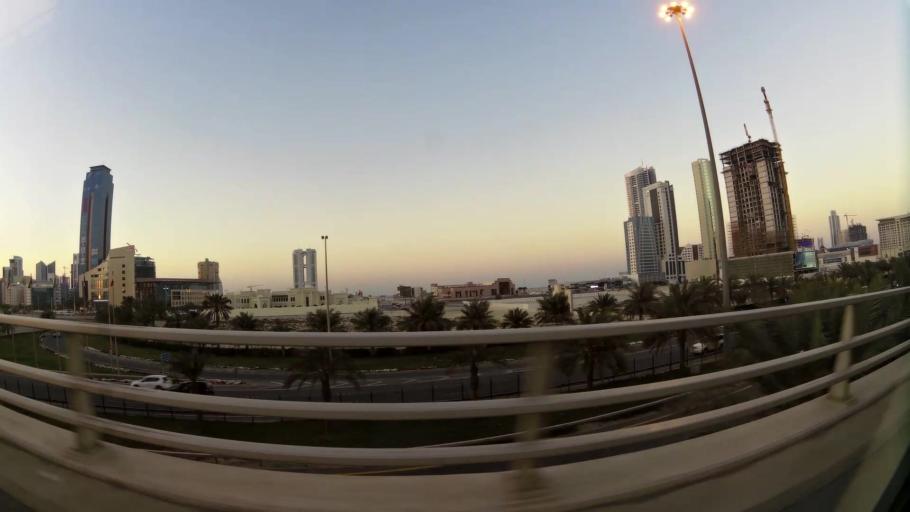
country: BH
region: Manama
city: Jidd Hafs
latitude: 26.2313
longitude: 50.5451
